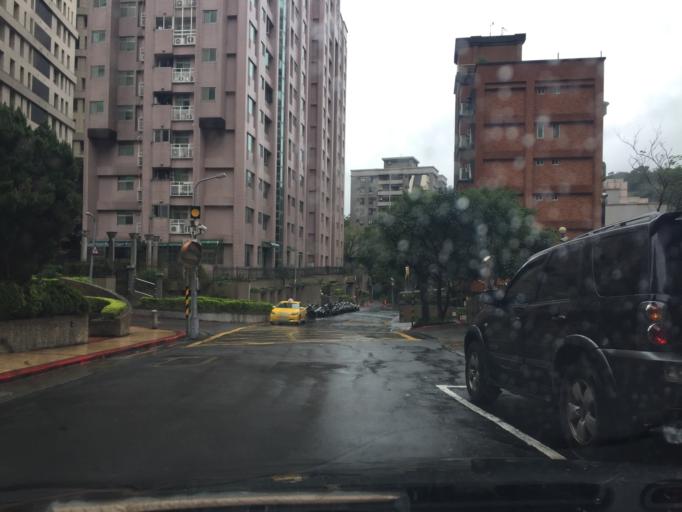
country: TW
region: Taipei
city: Taipei
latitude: 25.0805
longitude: 121.5975
